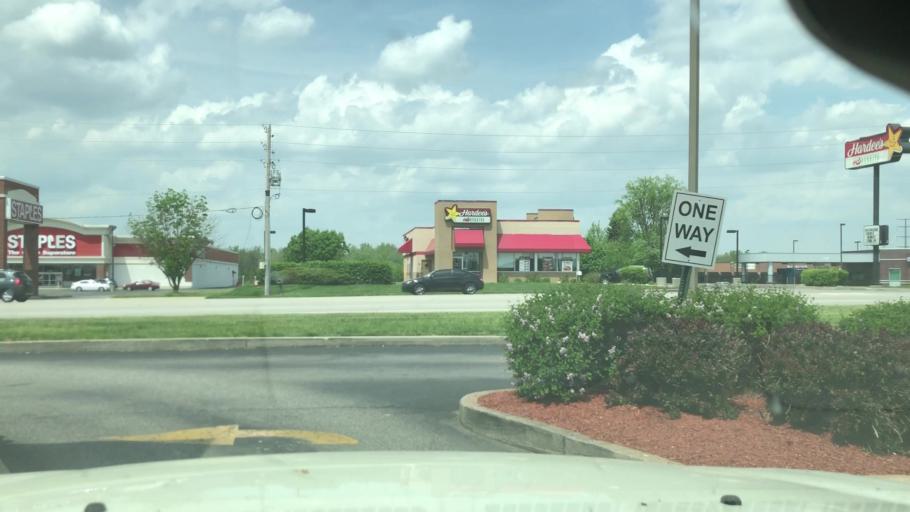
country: US
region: Indiana
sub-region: Marion County
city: Southport
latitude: 39.6656
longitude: -86.0806
